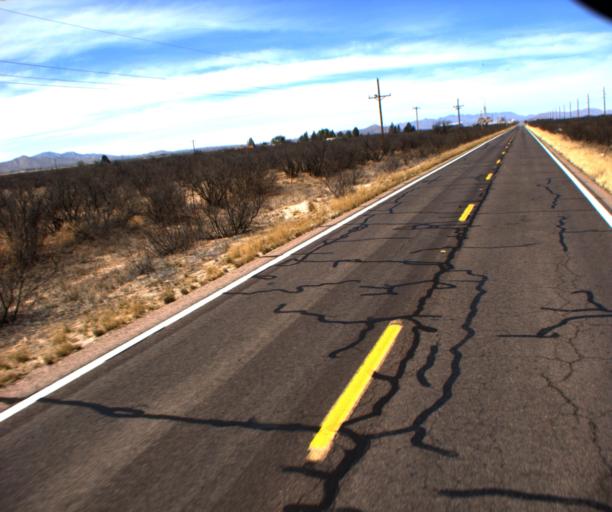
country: US
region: Arizona
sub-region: Cochise County
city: Willcox
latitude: 32.0273
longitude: -109.8746
